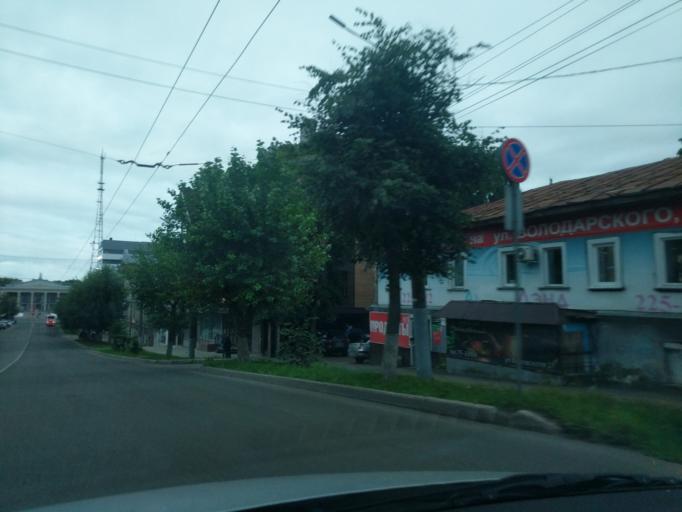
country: RU
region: Kirov
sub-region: Kirovo-Chepetskiy Rayon
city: Kirov
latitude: 58.5942
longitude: 49.6774
